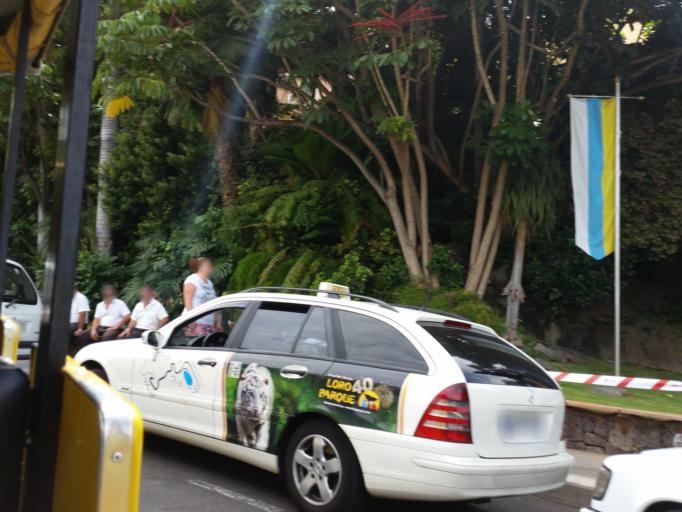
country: ES
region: Canary Islands
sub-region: Provincia de Santa Cruz de Tenerife
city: Puerto de la Cruz
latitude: 28.4085
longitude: -16.5662
